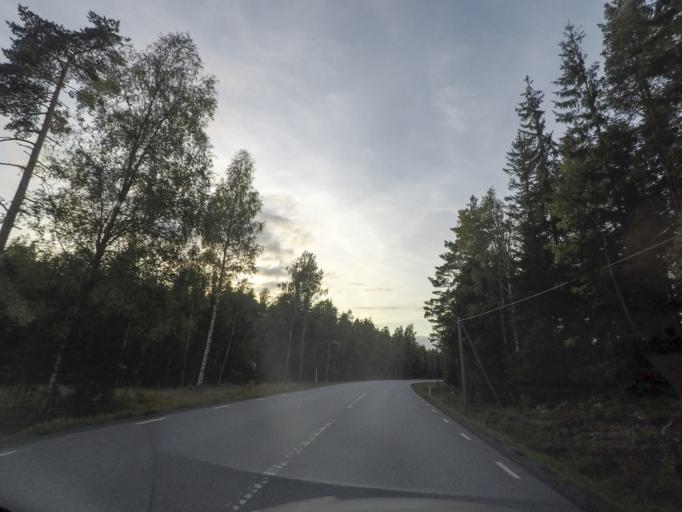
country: SE
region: OErebro
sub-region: Nora Kommun
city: As
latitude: 59.5551
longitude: 14.7477
